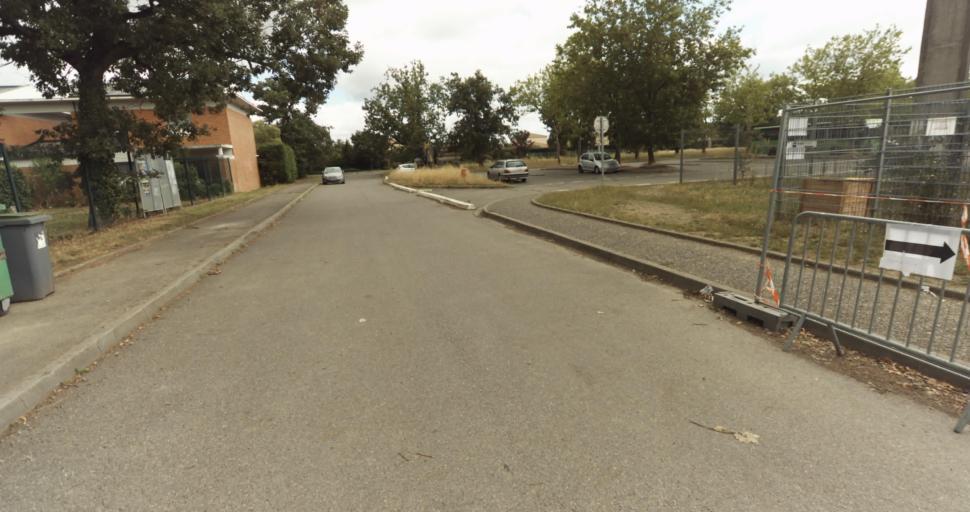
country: FR
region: Midi-Pyrenees
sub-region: Departement de la Haute-Garonne
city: Fonsorbes
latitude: 43.5517
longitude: 1.2321
